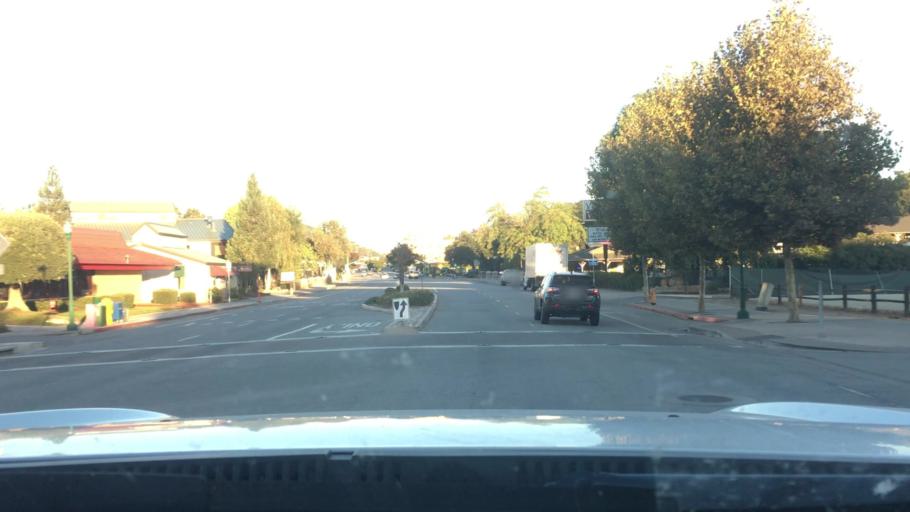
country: US
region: California
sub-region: San Luis Obispo County
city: Atascadero
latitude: 35.4870
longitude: -120.6659
